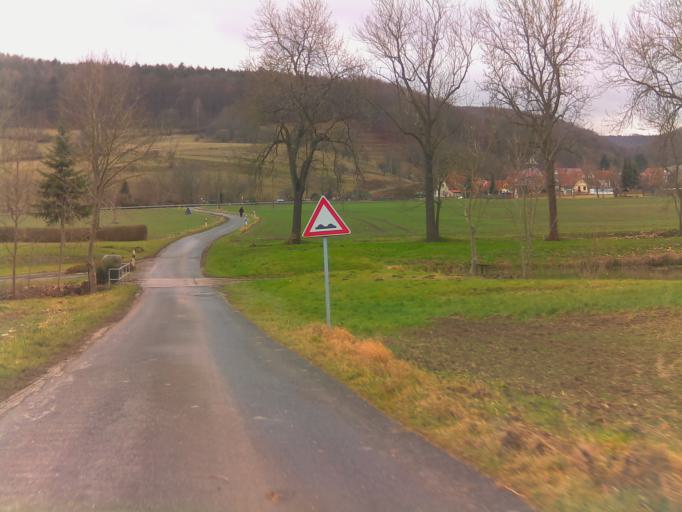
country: DE
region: Thuringia
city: Reinstadt
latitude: 50.8131
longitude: 11.4644
